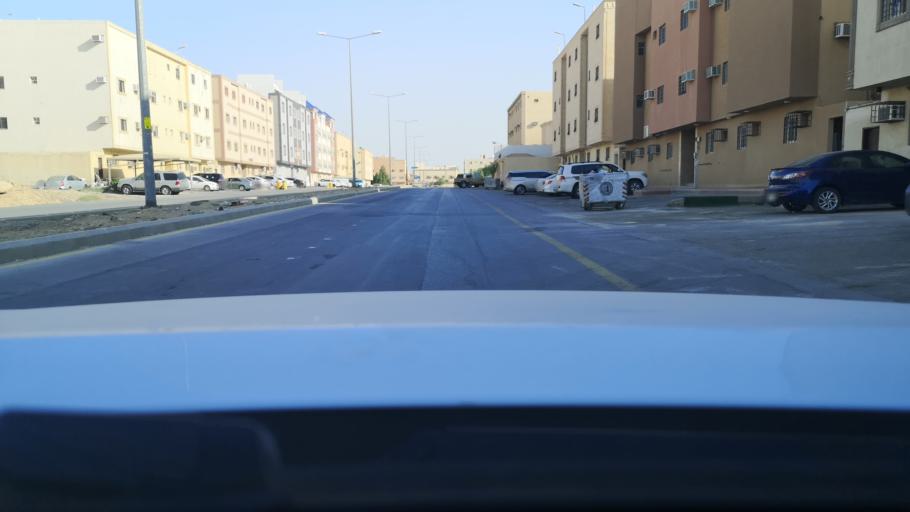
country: SA
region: Ar Riyad
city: Riyadh
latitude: 24.6392
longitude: 46.5534
